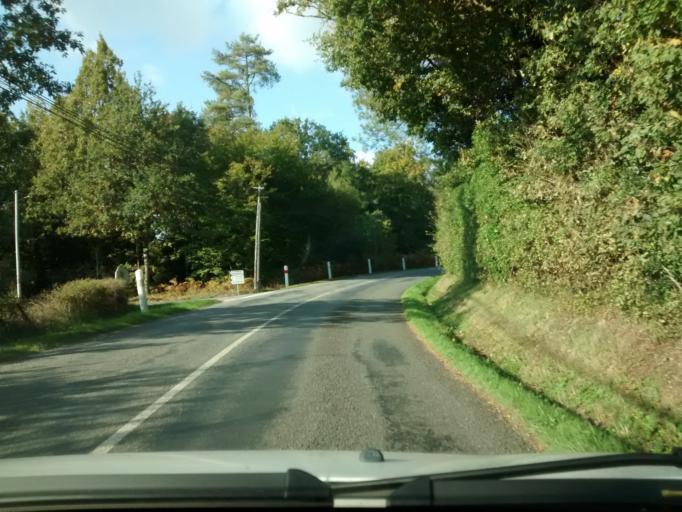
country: FR
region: Pays de la Loire
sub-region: Departement de la Loire-Atlantique
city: Sautron
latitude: 47.2731
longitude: -1.6721
